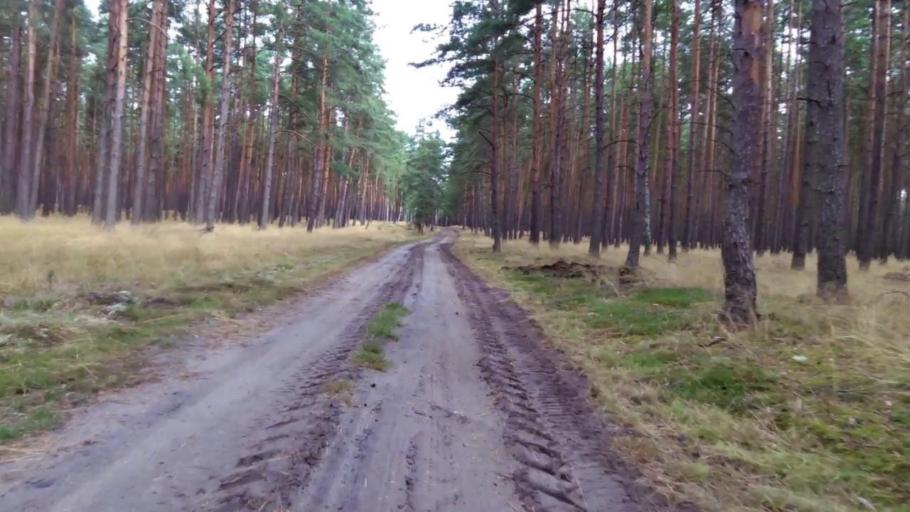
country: PL
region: West Pomeranian Voivodeship
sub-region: Powiat mysliborski
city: Debno
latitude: 52.8203
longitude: 14.6747
